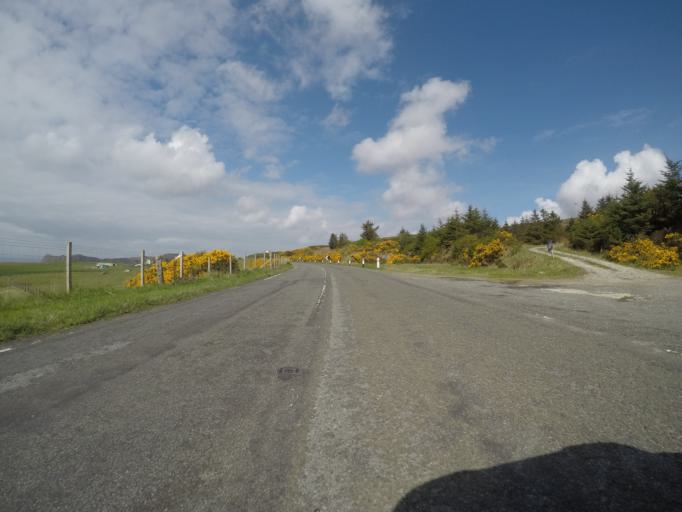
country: GB
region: Scotland
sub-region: Highland
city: Portree
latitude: 57.5714
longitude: -6.3640
